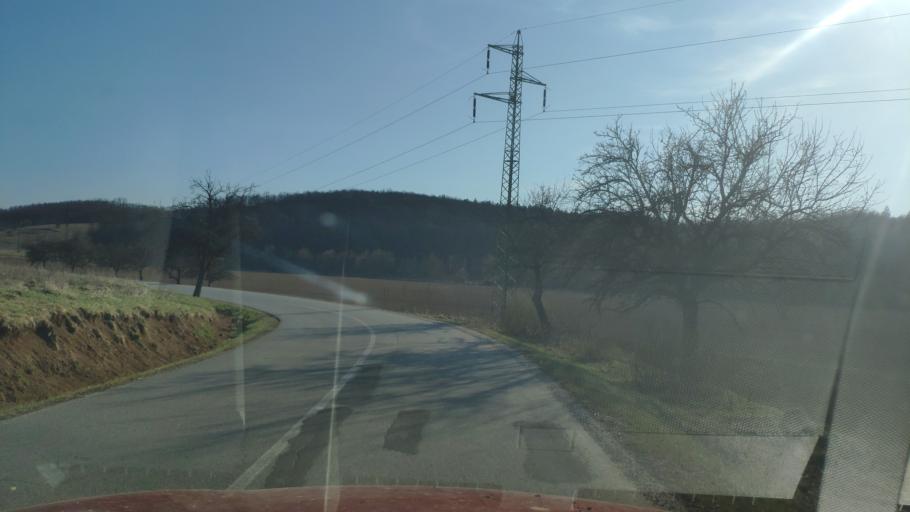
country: SK
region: Banskobystricky
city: Revuca
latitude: 48.5234
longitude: 20.2519
